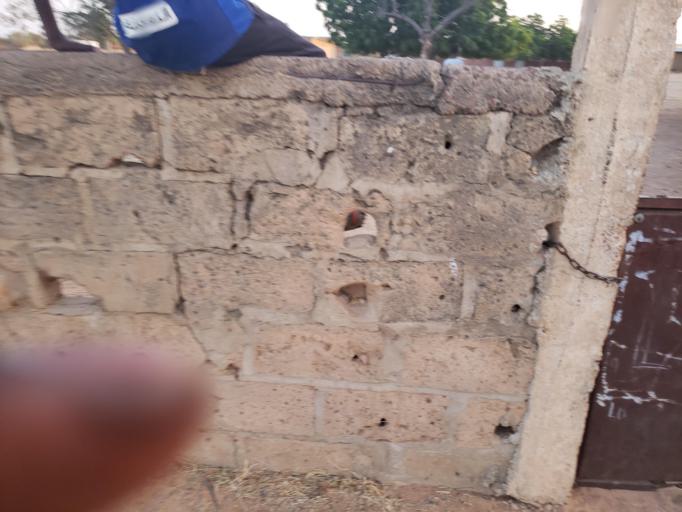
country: SN
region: Matam
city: Ranerou
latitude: 15.2950
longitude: -13.9629
